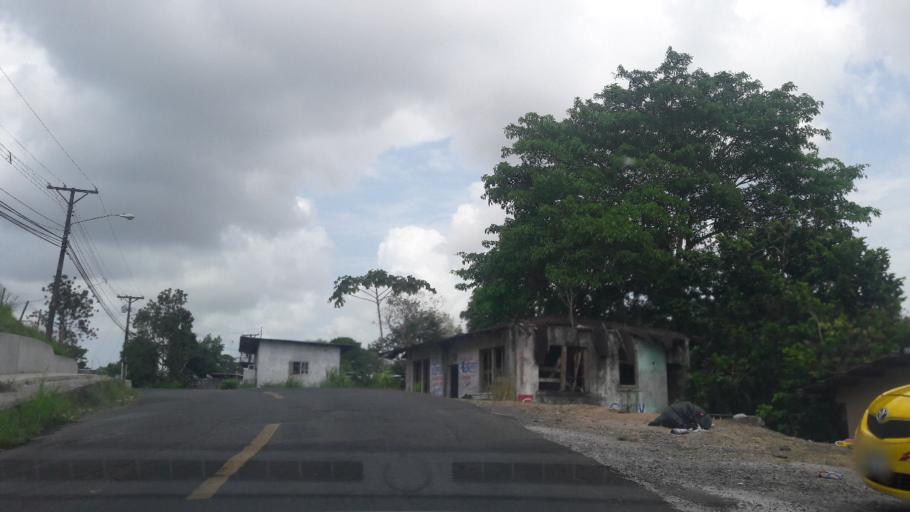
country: PA
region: Panama
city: Alcalde Diaz
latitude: 9.1146
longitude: -79.5553
